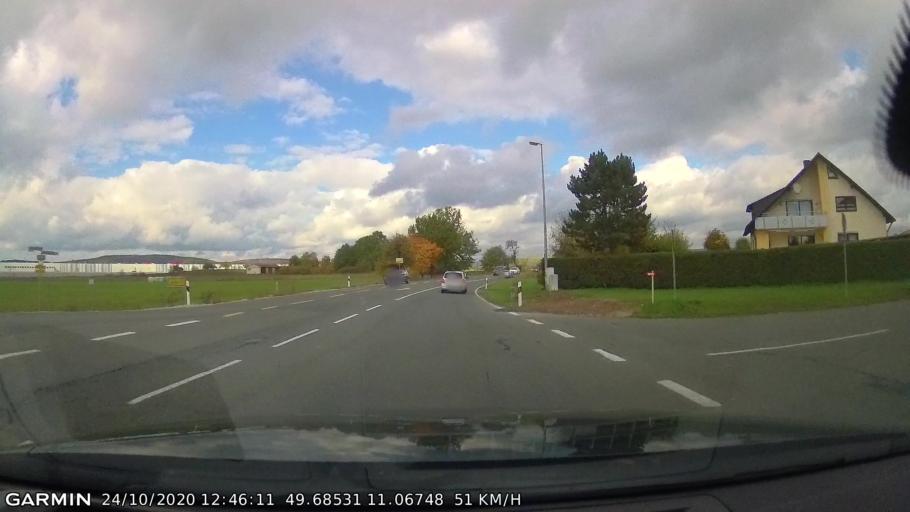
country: DE
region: Bavaria
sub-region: Upper Franconia
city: Poxdorf
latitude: 49.6854
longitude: 11.0674
